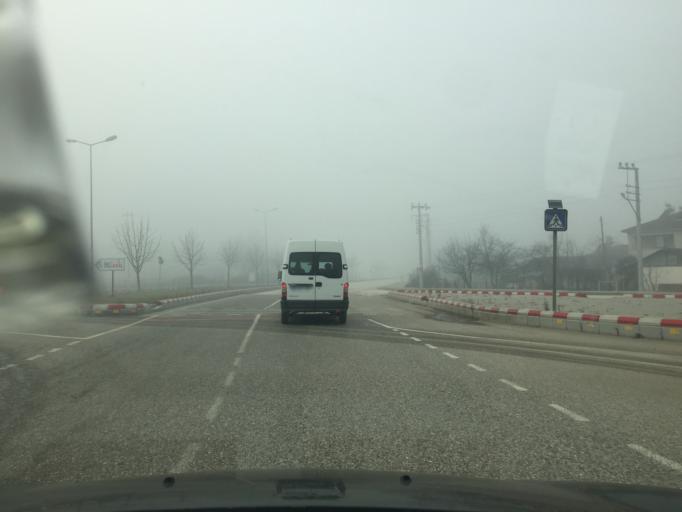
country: TR
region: Duzce
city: Duzce
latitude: 40.8413
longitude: 31.1801
